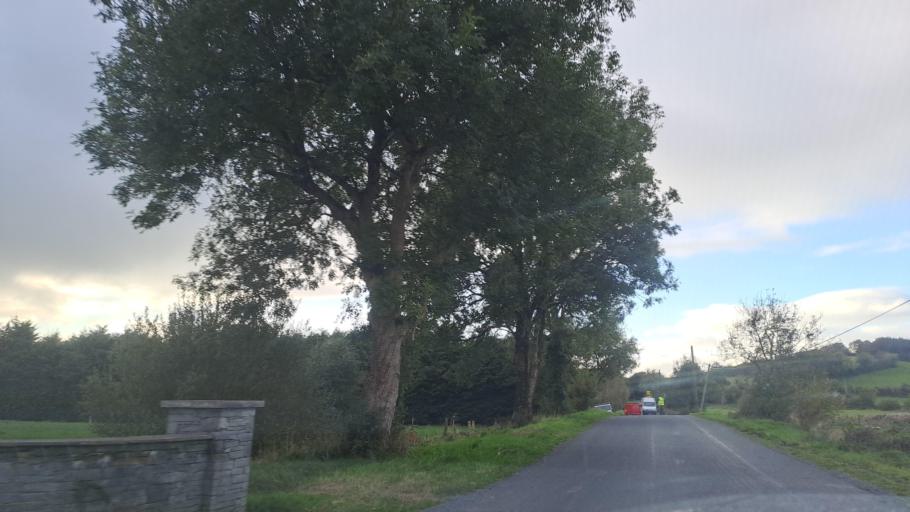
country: IE
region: Ulster
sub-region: County Monaghan
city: Castleblayney
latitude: 54.0390
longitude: -6.8258
